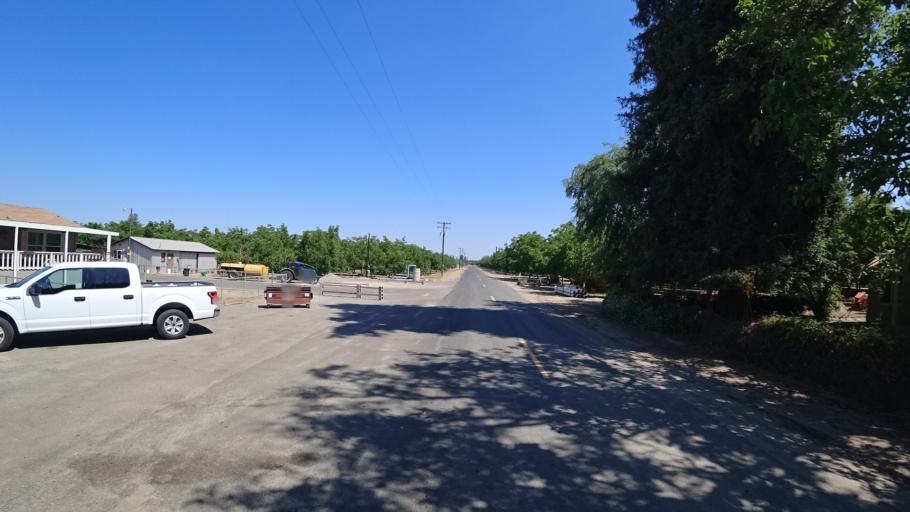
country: US
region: California
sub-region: Fresno County
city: Kingsburg
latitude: 36.4698
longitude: -119.5733
